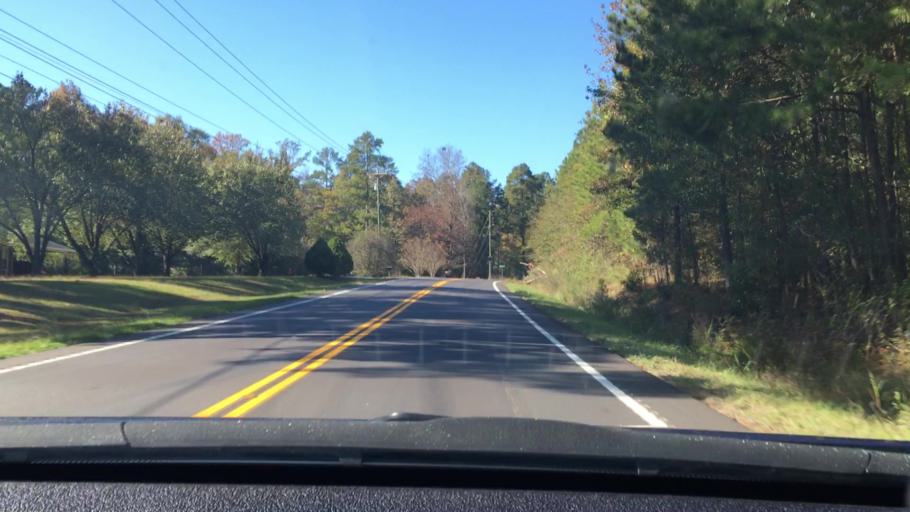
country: US
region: South Carolina
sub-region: Lexington County
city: Irmo
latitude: 34.1252
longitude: -81.1748
